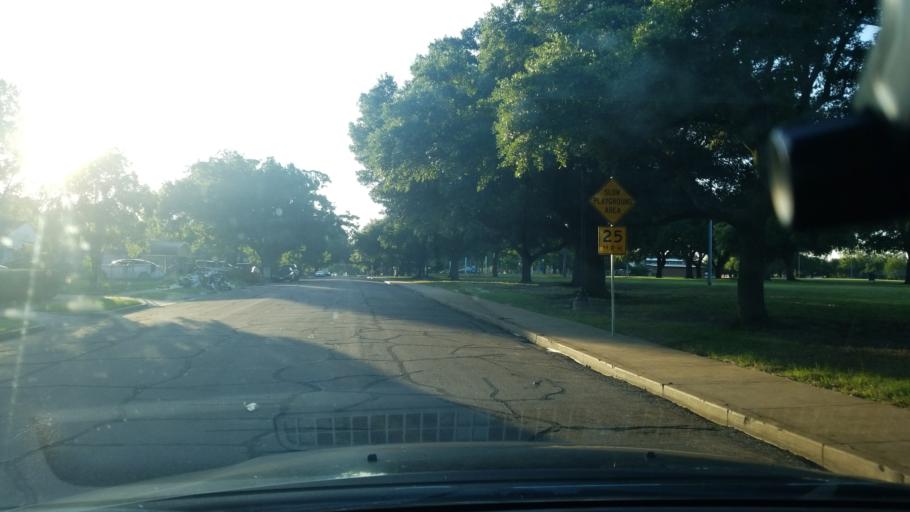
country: US
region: Texas
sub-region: Dallas County
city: Cockrell Hill
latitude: 32.7150
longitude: -96.8265
